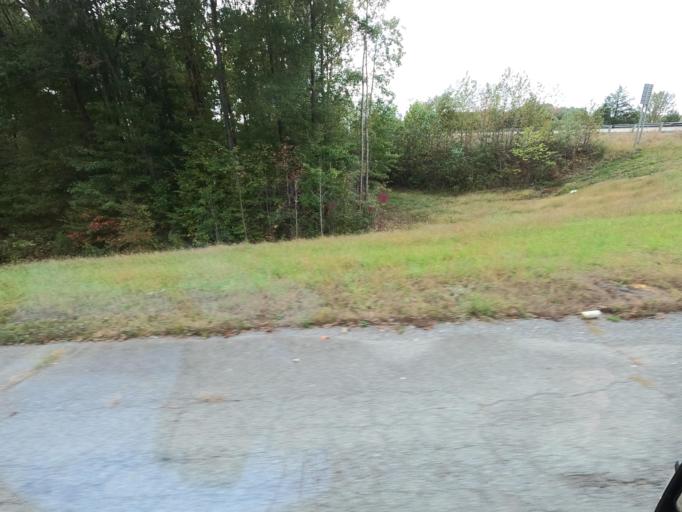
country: US
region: Tennessee
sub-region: Cheatham County
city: Pleasant View
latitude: 36.4516
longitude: -87.0982
